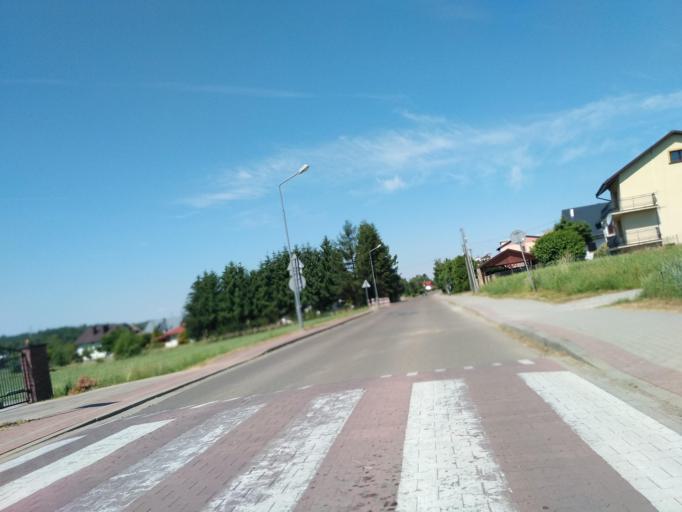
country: PL
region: Subcarpathian Voivodeship
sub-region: Powiat krosnienski
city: Korczyna
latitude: 49.7124
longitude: 21.8013
